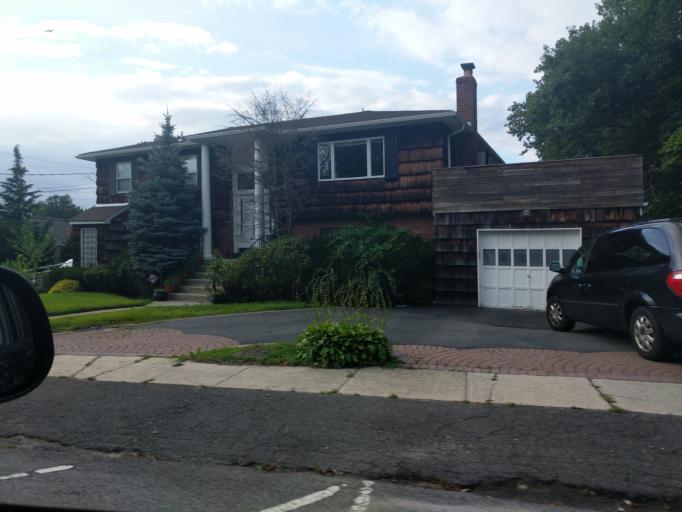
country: US
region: New York
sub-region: Nassau County
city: Hewlett Harbor
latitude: 40.6407
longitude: -73.6866
